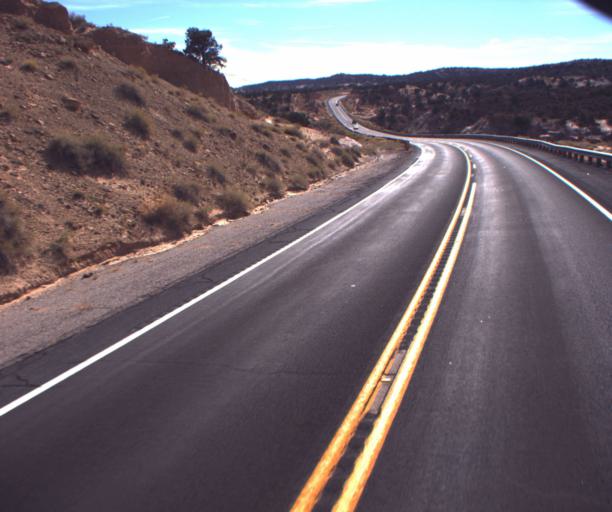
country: US
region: Arizona
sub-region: Coconino County
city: Kaibito
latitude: 36.6047
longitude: -110.9200
